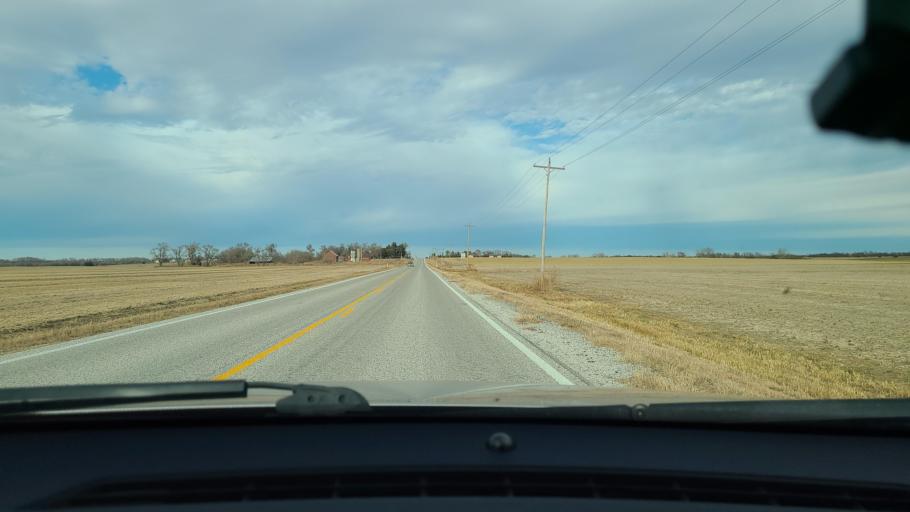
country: US
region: Kansas
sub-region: McPherson County
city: Inman
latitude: 38.2900
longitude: -97.9250
